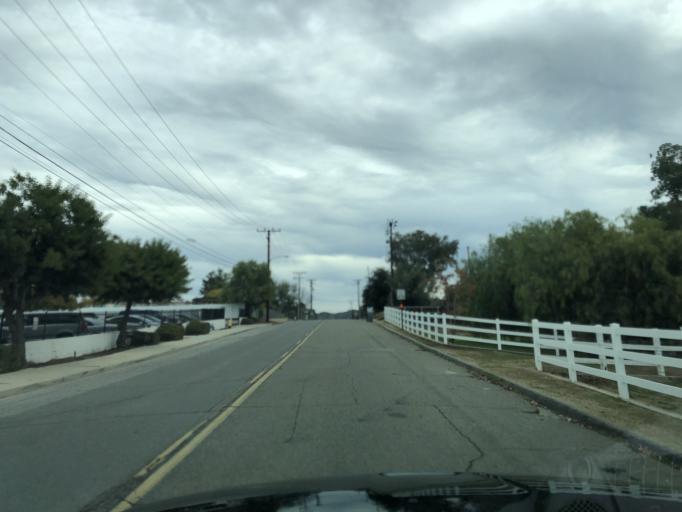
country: US
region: California
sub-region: Riverside County
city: Wildomar
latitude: 33.6196
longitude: -117.2871
